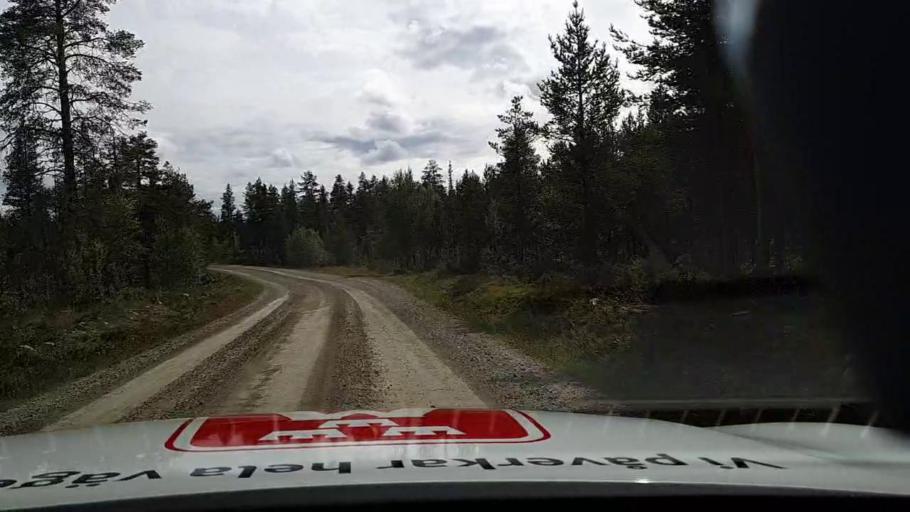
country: SE
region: Jaemtland
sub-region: Are Kommun
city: Jarpen
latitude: 62.5166
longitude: 13.4879
